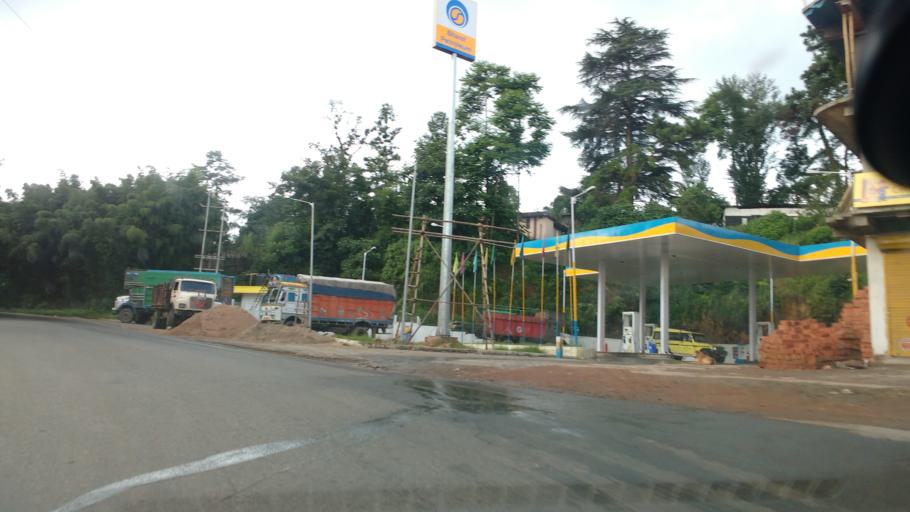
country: IN
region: Meghalaya
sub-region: East Khasi Hills
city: Shillong
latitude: 25.5631
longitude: 91.8537
